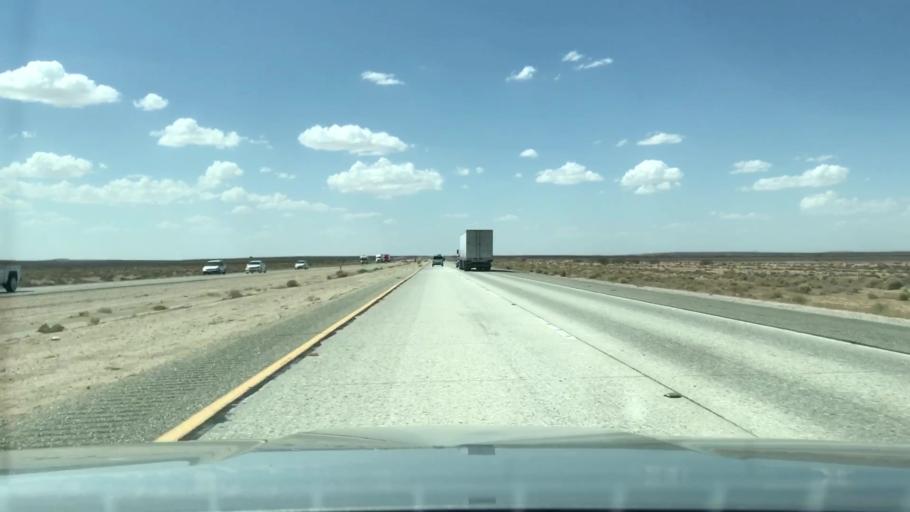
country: US
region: California
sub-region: Kern County
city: Boron
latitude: 34.9372
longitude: -117.3798
